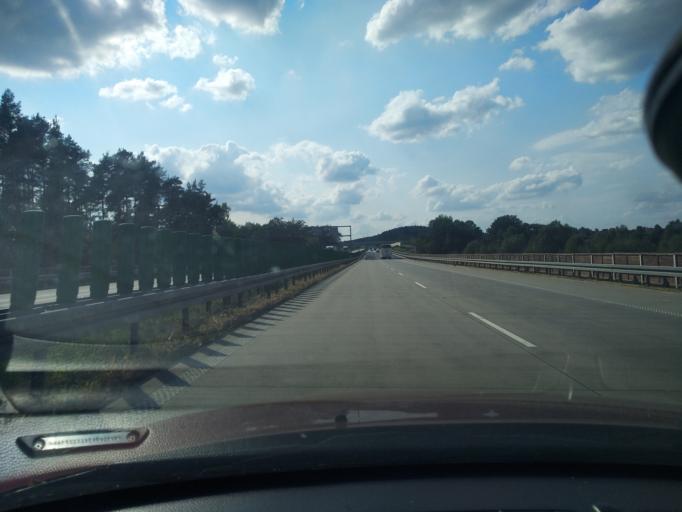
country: PL
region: Lower Silesian Voivodeship
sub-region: Powiat boleslawiecki
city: Nowogrodziec
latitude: 51.2685
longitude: 15.4187
